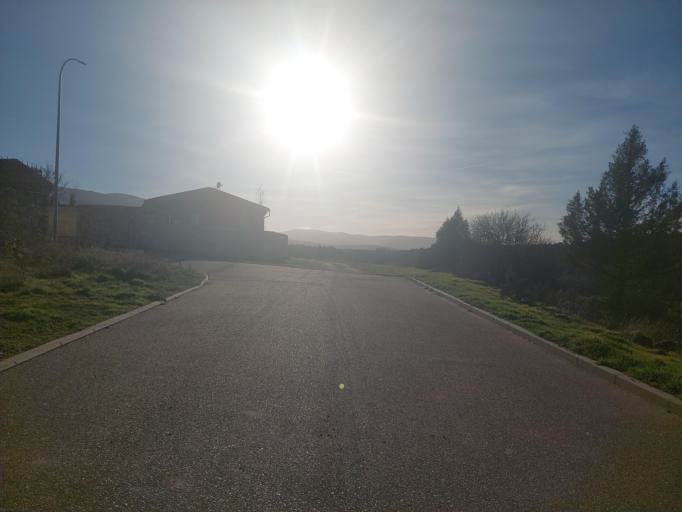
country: ES
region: Castille and Leon
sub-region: Provincia de Segovia
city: Pradena
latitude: 41.1360
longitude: -3.6935
